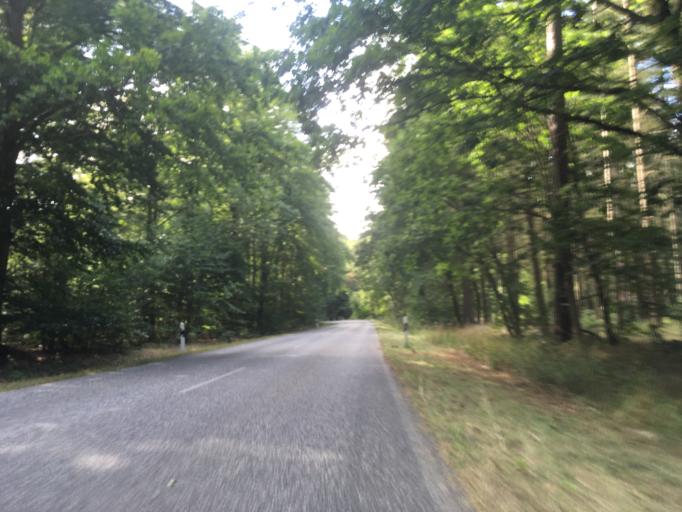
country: DE
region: Brandenburg
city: Chorin
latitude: 52.9155
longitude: 13.9197
